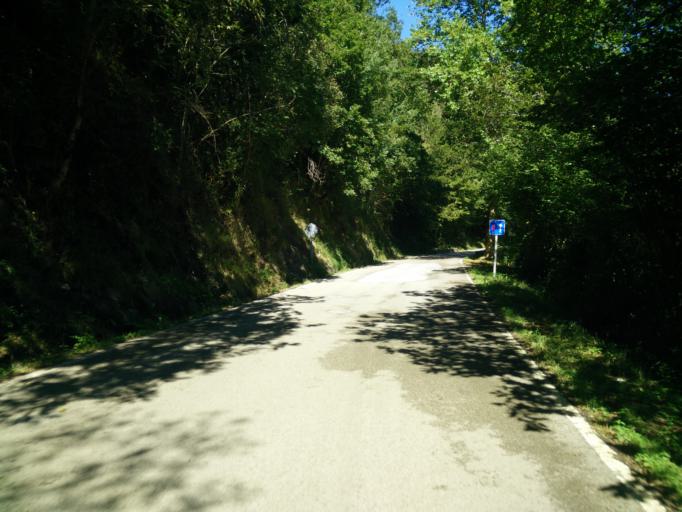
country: ES
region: Cantabria
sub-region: Provincia de Cantabria
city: Ruente
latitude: 43.1469
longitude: -4.2877
